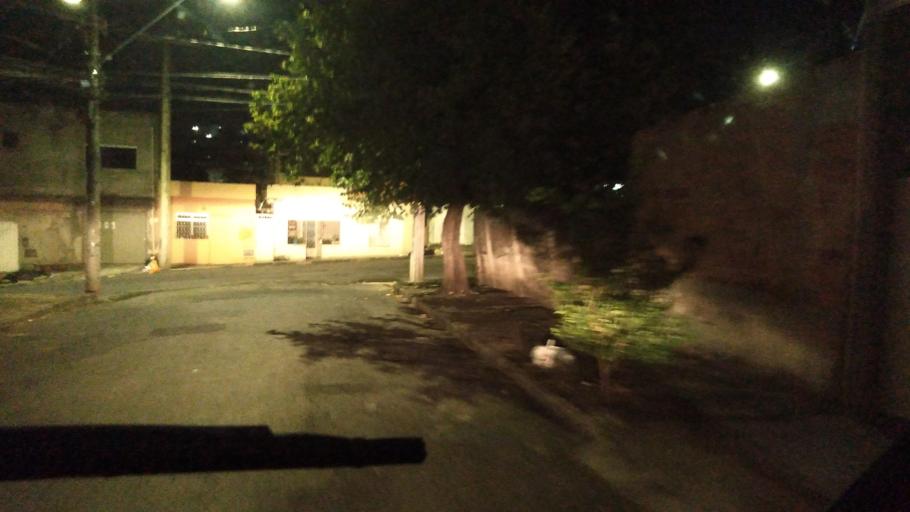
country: BR
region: Minas Gerais
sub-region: Belo Horizonte
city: Belo Horizonte
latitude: -19.8742
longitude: -43.9413
